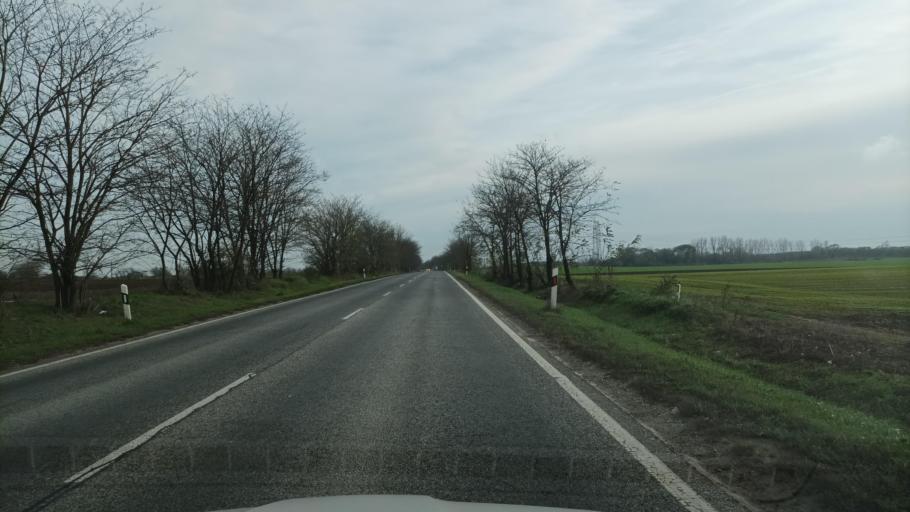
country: HU
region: Pest
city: Ocsa
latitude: 47.3204
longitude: 19.1976
